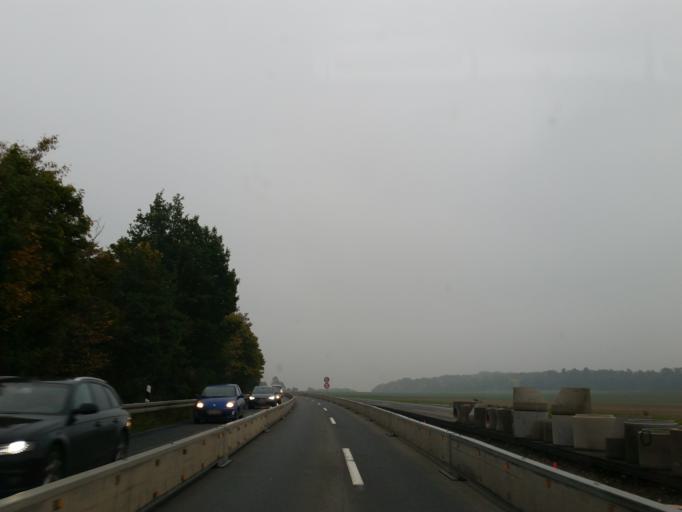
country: DE
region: Lower Saxony
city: Vienenburg
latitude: 51.9718
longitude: 10.5647
